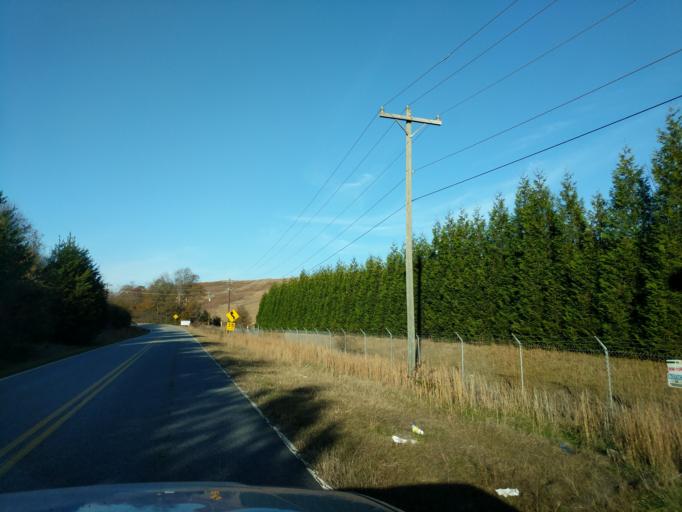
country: US
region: South Carolina
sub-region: Spartanburg County
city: Wellford
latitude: 34.9261
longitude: -82.0792
